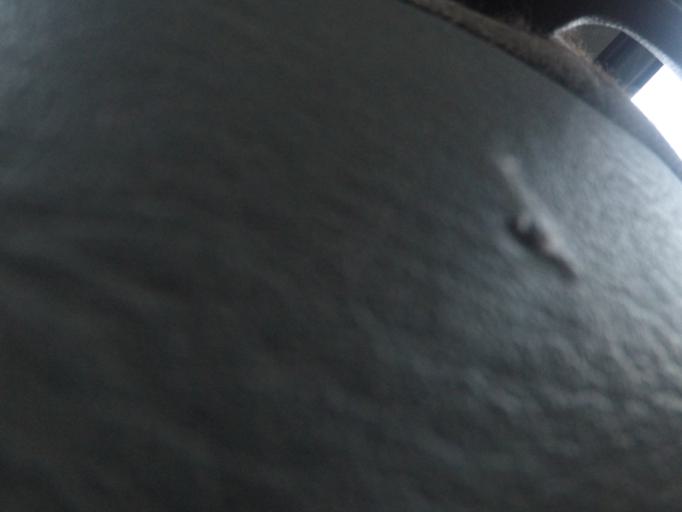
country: US
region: Alaska
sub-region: Juneau City and Borough
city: Juneau
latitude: 58.2997
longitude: -134.6689
